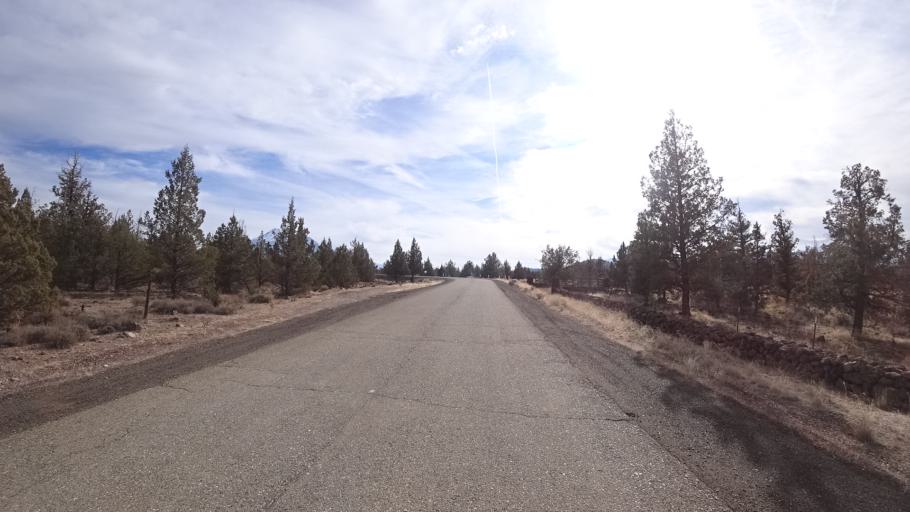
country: US
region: California
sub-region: Siskiyou County
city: Weed
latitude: 41.5917
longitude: -122.4008
